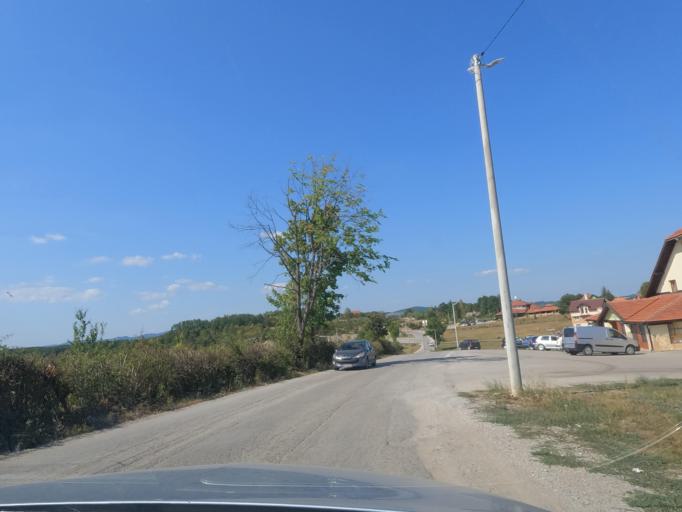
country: RS
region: Central Serbia
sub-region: Zlatiborski Okrug
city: Cajetina
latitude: 43.7896
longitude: 19.7656
